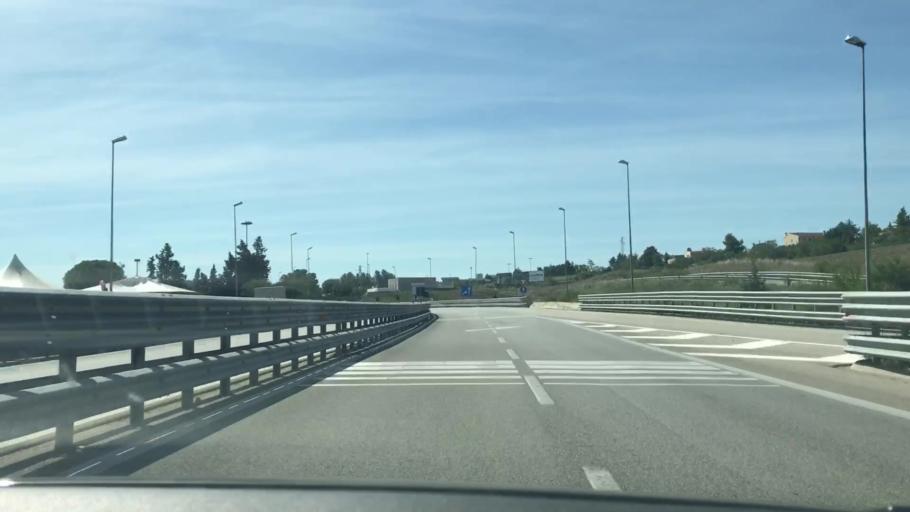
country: IT
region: Basilicate
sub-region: Provincia di Matera
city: Matera
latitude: 40.6900
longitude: 16.5906
